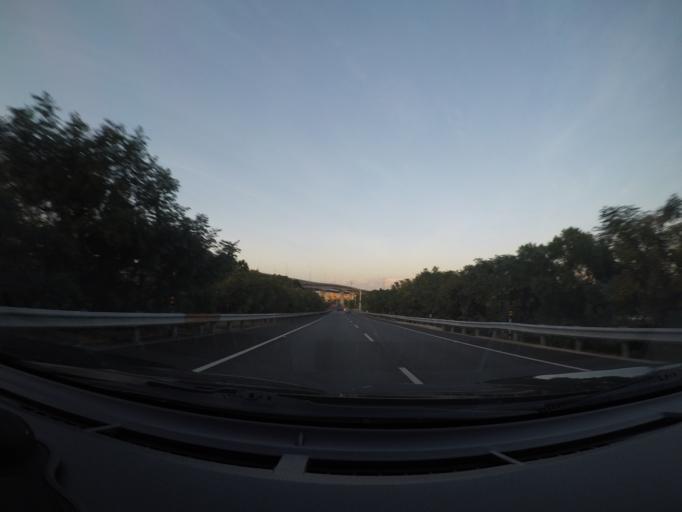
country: TW
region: Taiwan
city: Taoyuan City
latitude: 25.0195
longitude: 121.2769
